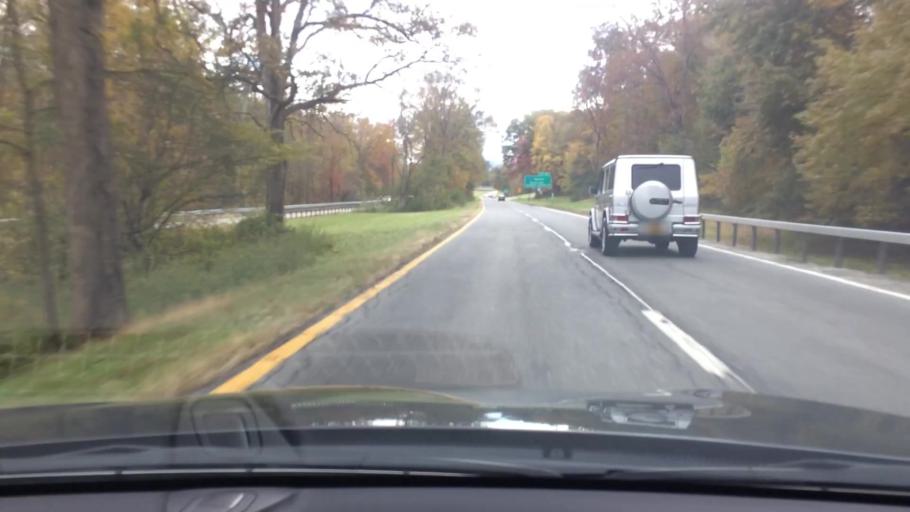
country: US
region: New York
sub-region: Dutchess County
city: Hillside Lake
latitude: 41.6008
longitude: -73.7640
